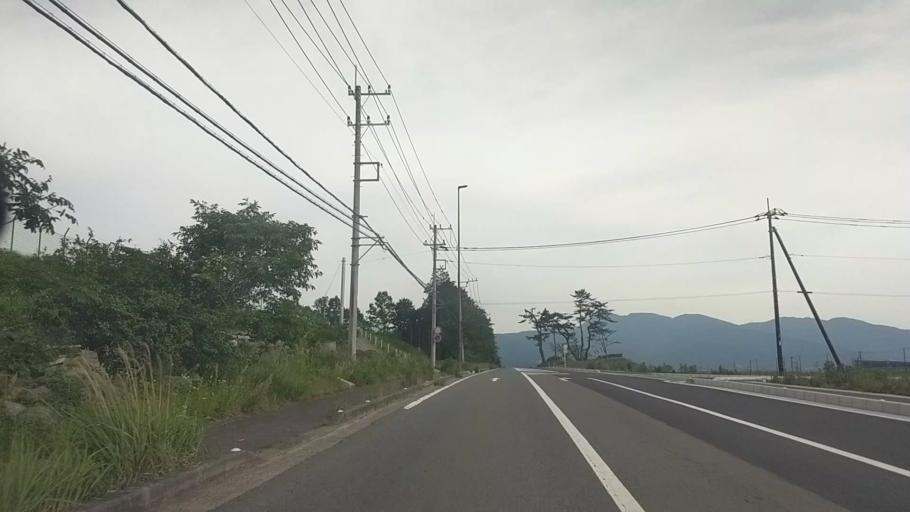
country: JP
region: Shizuoka
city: Gotemba
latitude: 35.3683
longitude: 138.9647
